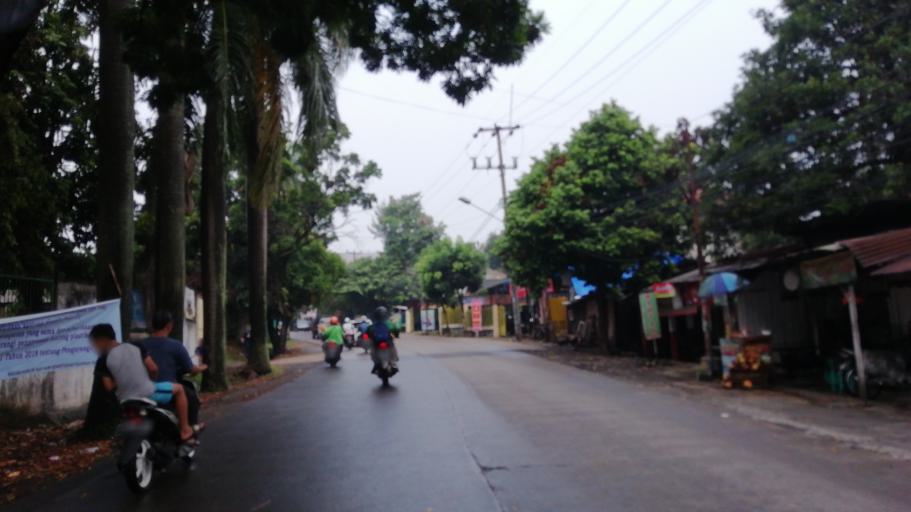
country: ID
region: West Java
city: Bogor
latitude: -6.5547
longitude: 106.8092
